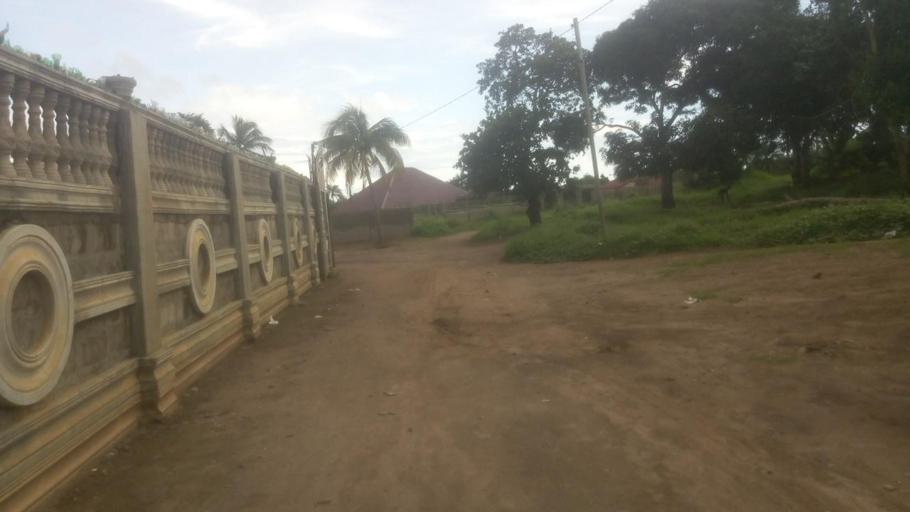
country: SL
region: Northern Province
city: Masoyila
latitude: 8.5852
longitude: -13.1667
